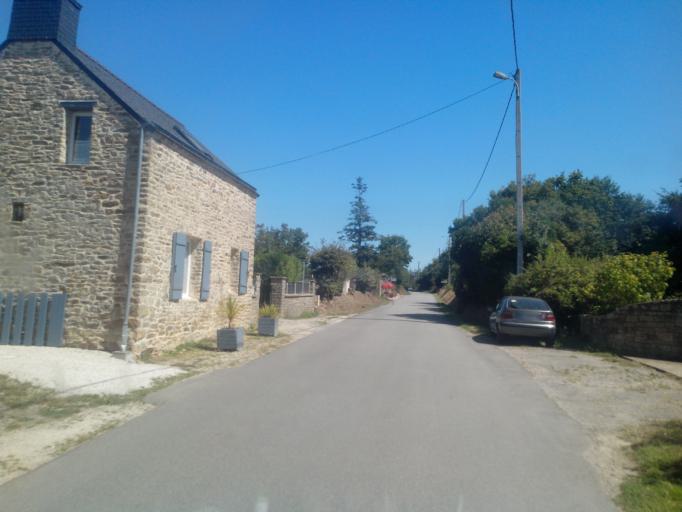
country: FR
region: Brittany
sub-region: Departement du Morbihan
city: Molac
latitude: 47.7308
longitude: -2.4335
